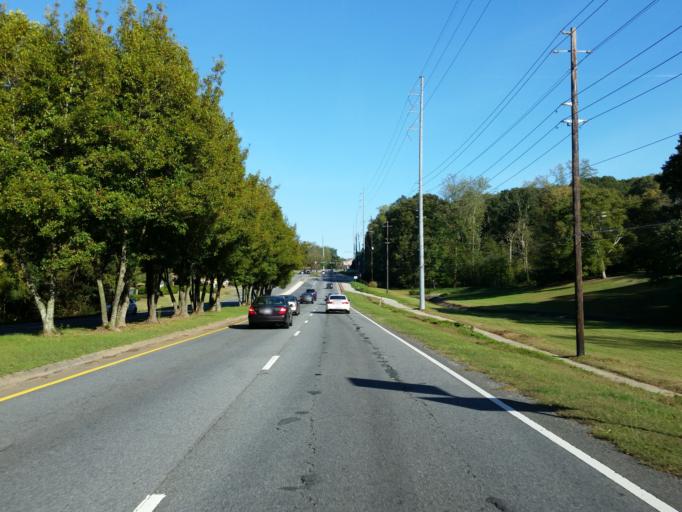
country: US
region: Georgia
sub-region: Fulton County
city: Sandy Springs
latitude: 33.9791
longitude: -84.4510
